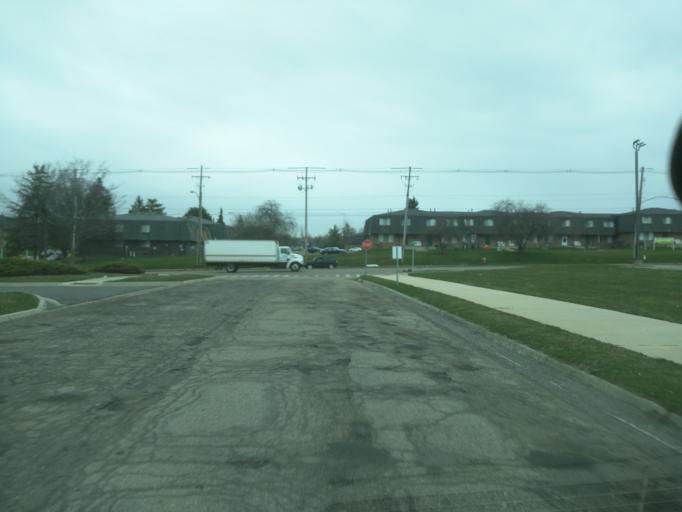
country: US
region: Michigan
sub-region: Ingham County
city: Holt
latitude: 42.6823
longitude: -84.5172
